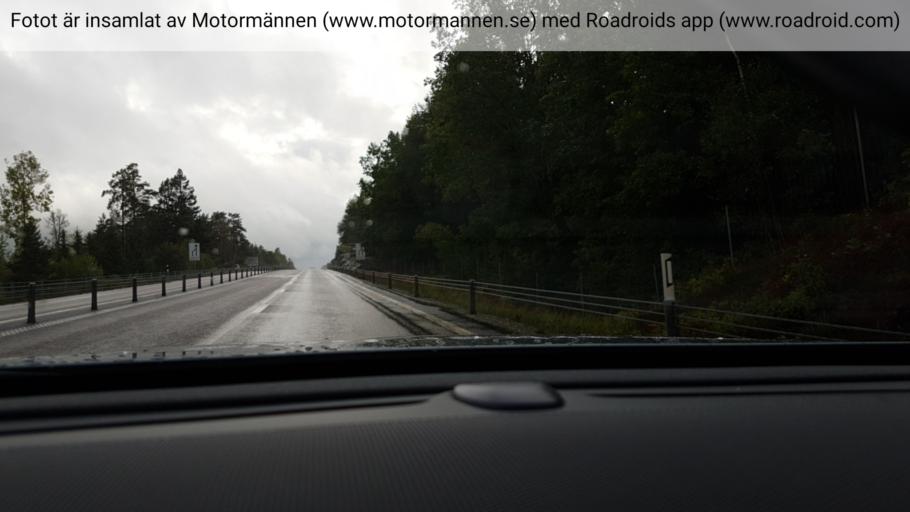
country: SE
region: Vaestra Goetaland
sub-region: Melleruds Kommun
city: Mellerud
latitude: 58.7510
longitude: 12.4854
